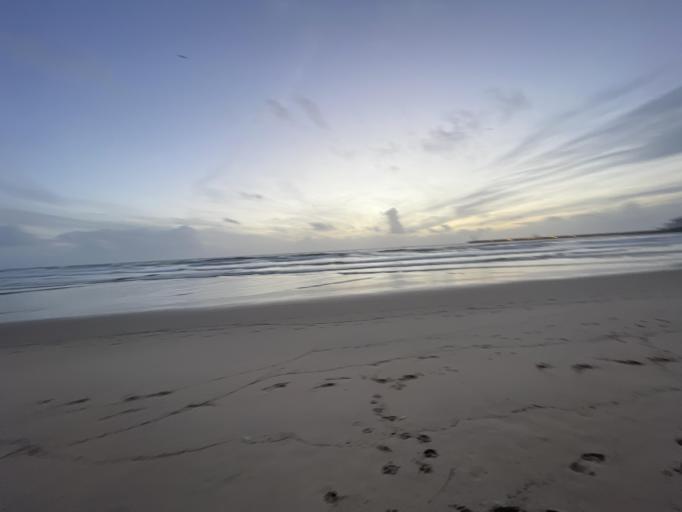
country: PT
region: Porto
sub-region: Matosinhos
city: Matosinhos
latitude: 41.1740
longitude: -8.6910
